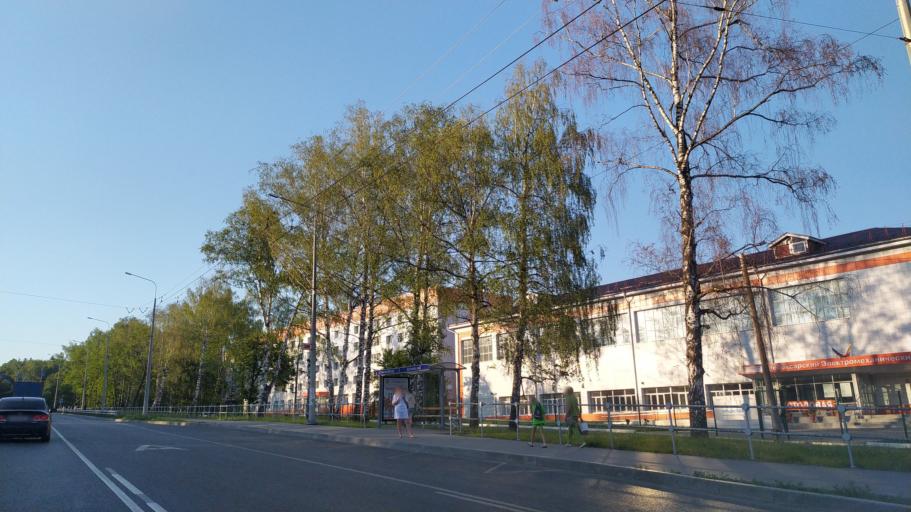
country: RU
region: Chuvashia
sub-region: Cheboksarskiy Rayon
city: Cheboksary
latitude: 56.0868
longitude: 47.2680
